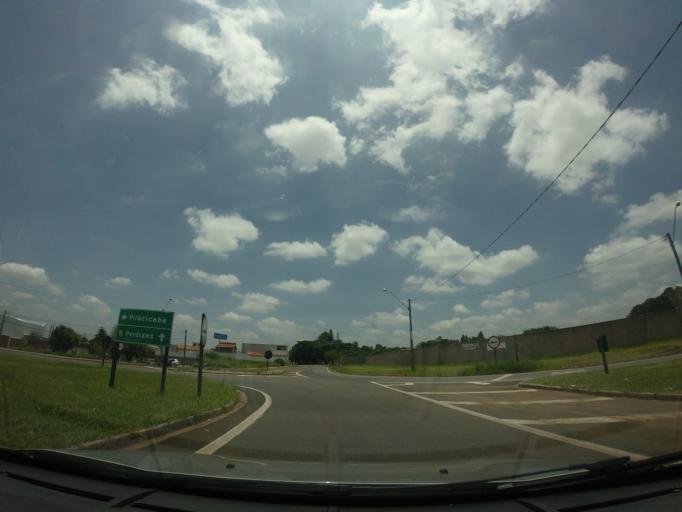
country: BR
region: Sao Paulo
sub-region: Piracicaba
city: Piracicaba
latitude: -22.7654
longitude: -47.5943
